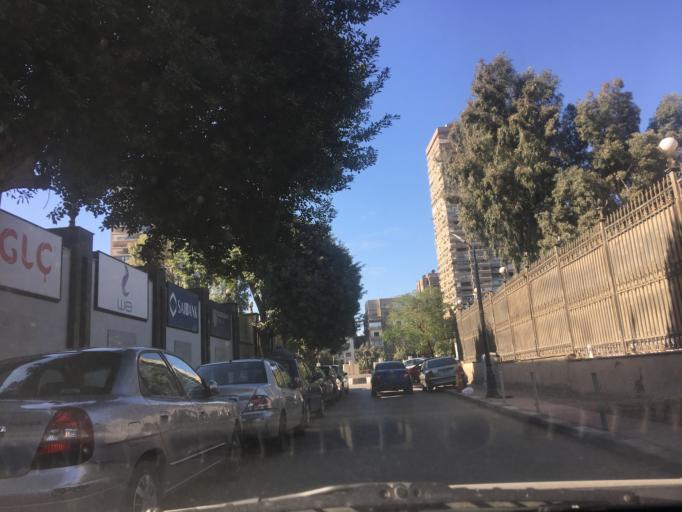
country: EG
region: Muhafazat al Qahirah
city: Cairo
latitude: 30.0463
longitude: 31.2205
